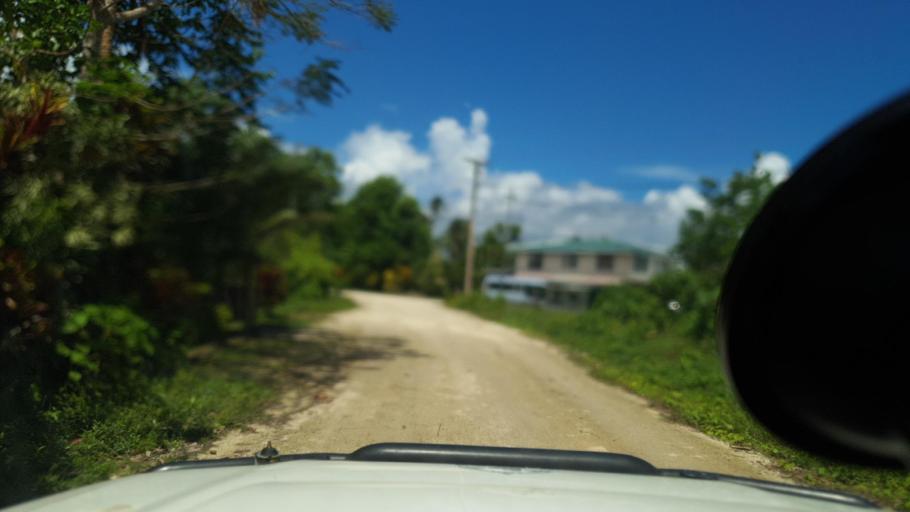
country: SB
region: Western Province
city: Gizo
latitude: -8.3290
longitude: 157.2762
